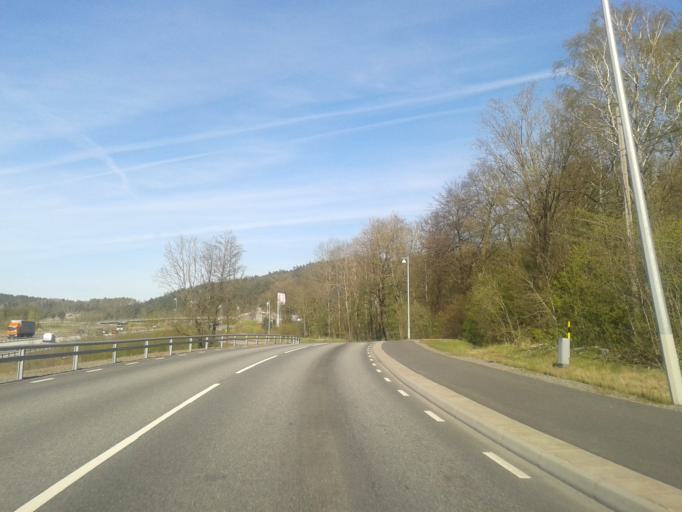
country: SE
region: Vaestra Goetaland
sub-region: Ale Kommun
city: Surte
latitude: 57.8686
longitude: 12.0264
